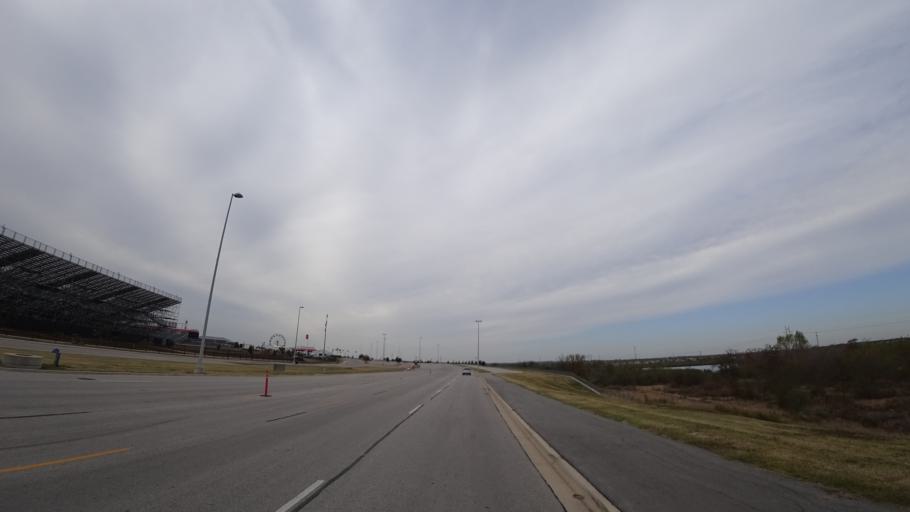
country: US
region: Texas
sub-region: Travis County
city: Garfield
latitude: 30.1386
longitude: -97.6354
